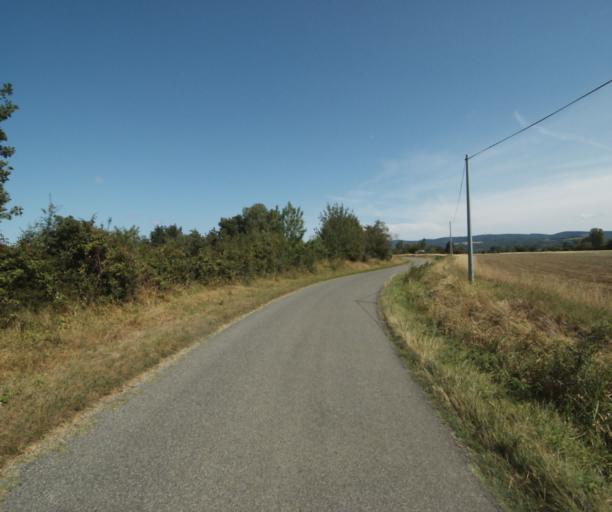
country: FR
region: Midi-Pyrenees
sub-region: Departement de la Haute-Garonne
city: Revel
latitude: 43.4791
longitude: 1.9745
